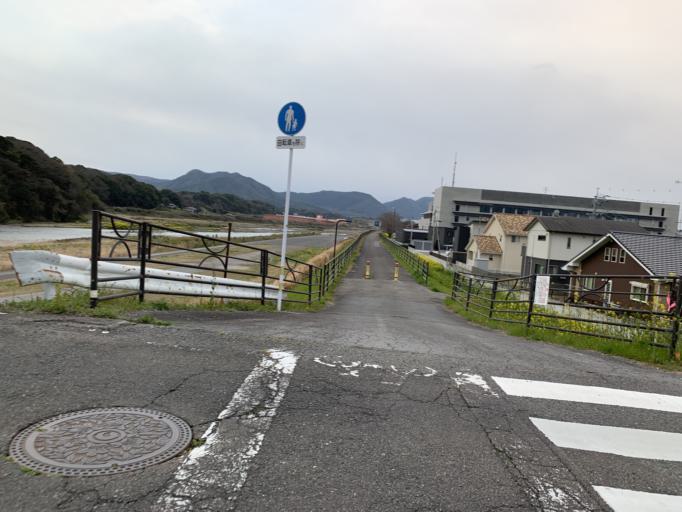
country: JP
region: Oita
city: Bungo-Takada-shi
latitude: 33.5341
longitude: 131.3515
